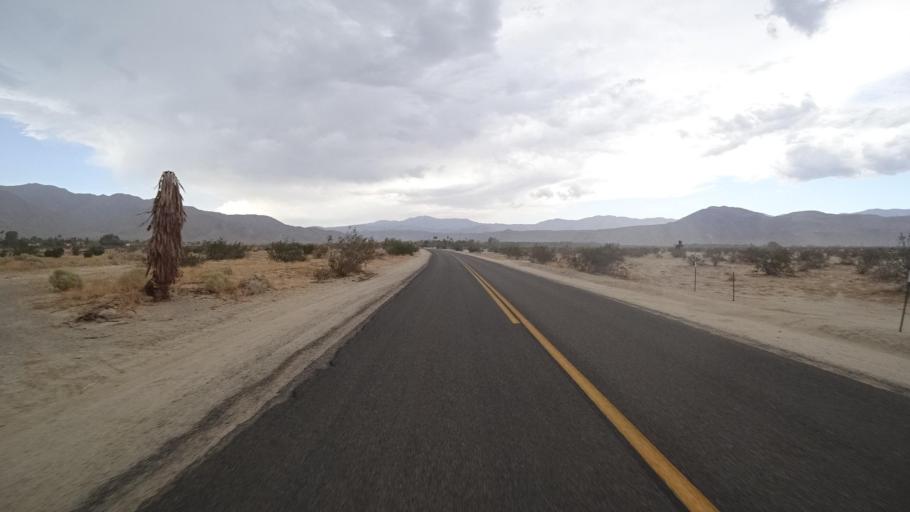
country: US
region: California
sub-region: San Diego County
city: Borrego Springs
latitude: 33.2867
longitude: -116.3754
